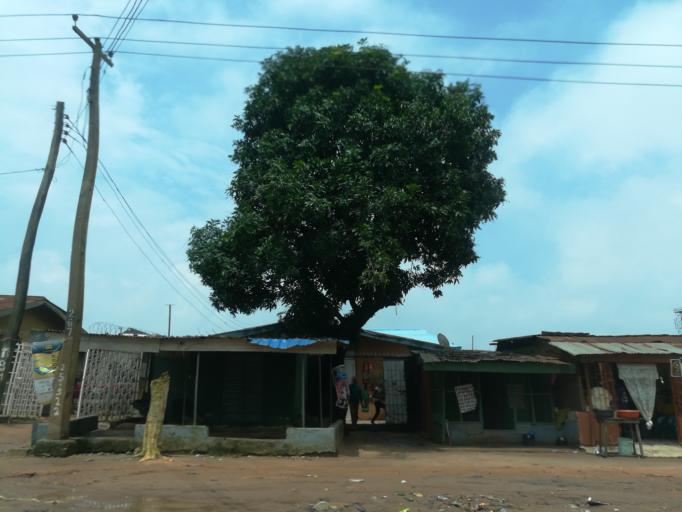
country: NG
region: Lagos
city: Ikorodu
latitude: 6.6655
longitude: 3.5170
